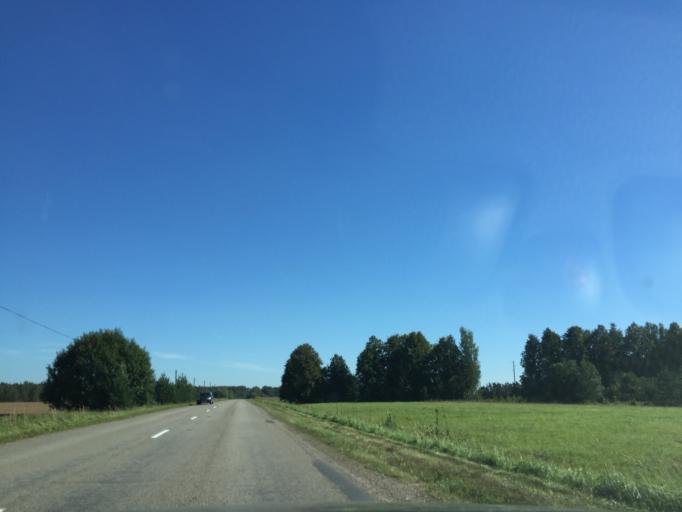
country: LV
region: Akniste
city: Akniste
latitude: 56.1451
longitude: 25.7966
